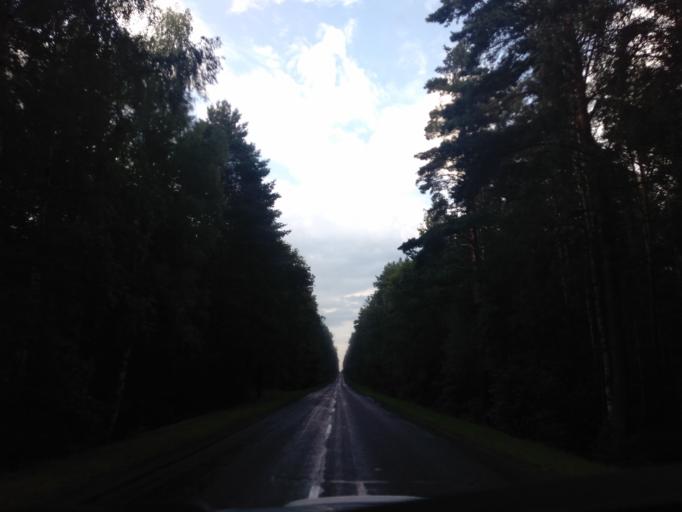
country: BY
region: Minsk
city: Uzda
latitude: 53.3596
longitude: 27.1000
